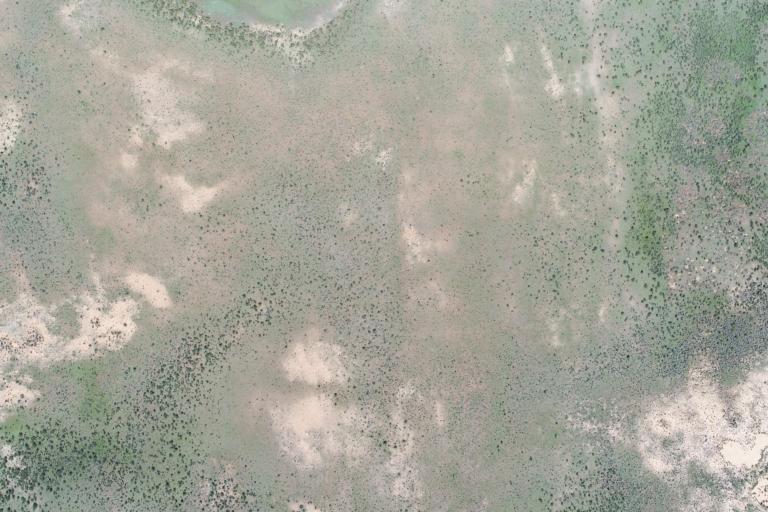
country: BO
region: La Paz
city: Curahuara de Carangas
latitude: -17.2930
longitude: -68.5206
